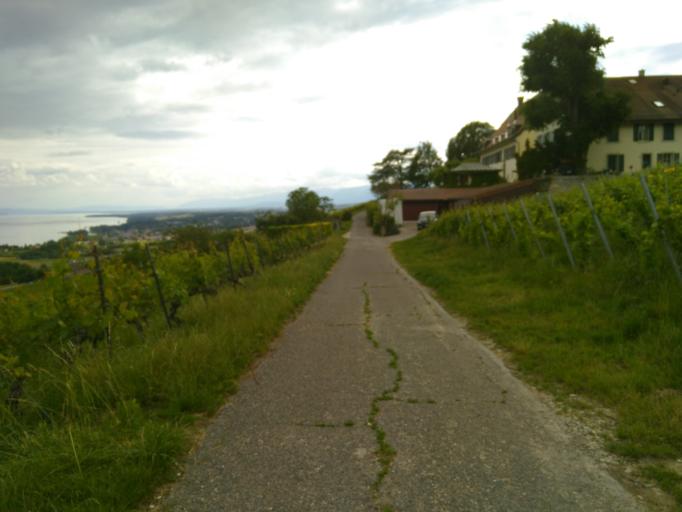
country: CH
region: Vaud
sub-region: Nyon District
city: Perroy
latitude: 46.4785
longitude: 6.3613
